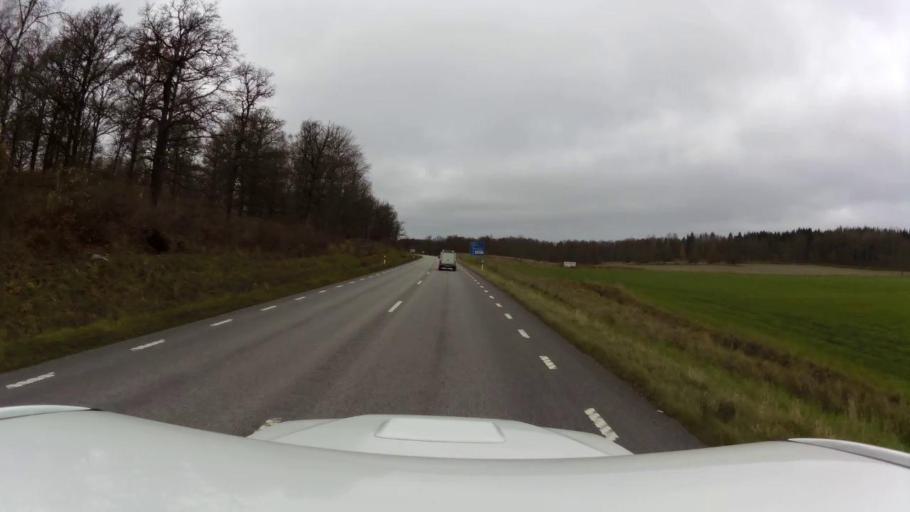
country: SE
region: OEstergoetland
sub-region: Kinda Kommun
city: Rimforsa
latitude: 58.2066
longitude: 15.6688
